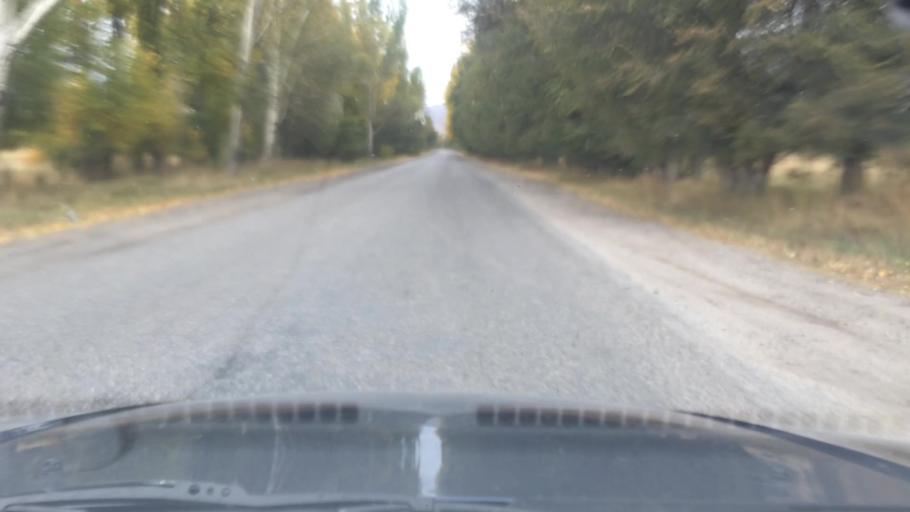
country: KG
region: Ysyk-Koel
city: Tyup
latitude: 42.7814
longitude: 78.2264
